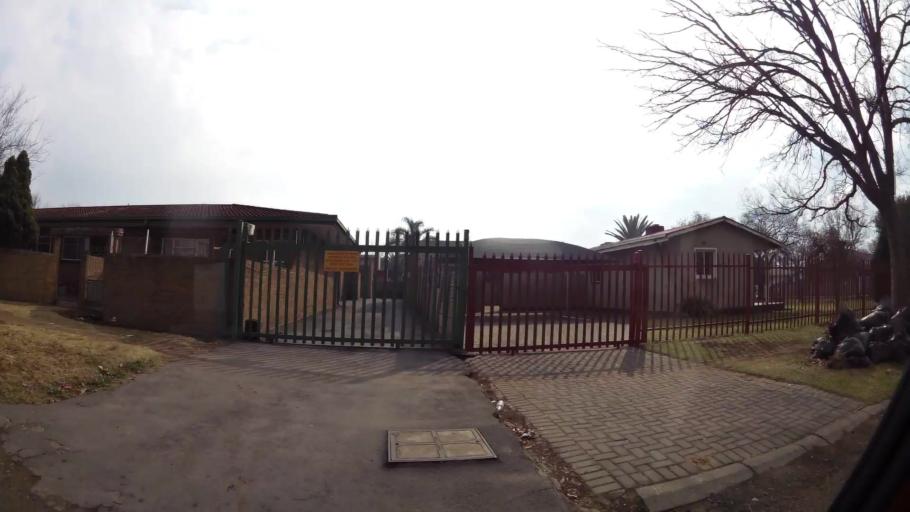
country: ZA
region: Gauteng
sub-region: Sedibeng District Municipality
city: Vanderbijlpark
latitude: -26.6887
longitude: 27.8356
